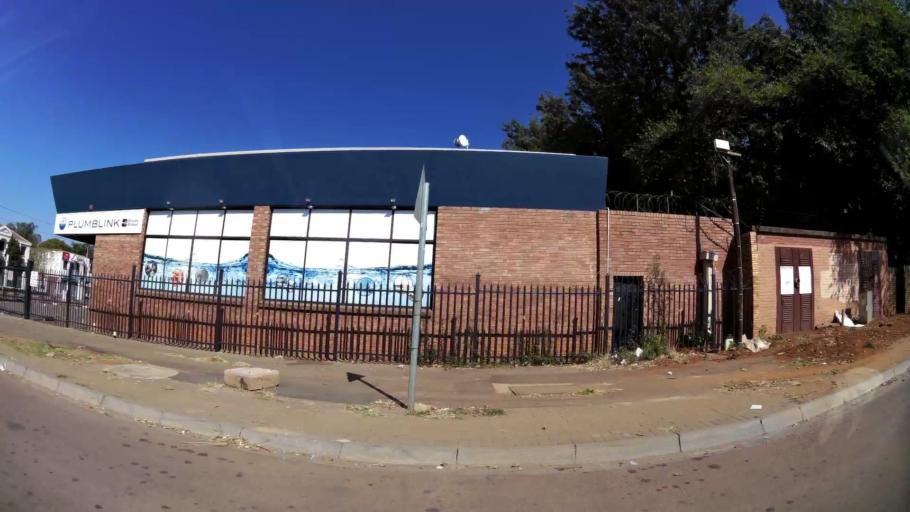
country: ZA
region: Gauteng
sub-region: City of Tshwane Metropolitan Municipality
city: Pretoria
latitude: -25.7584
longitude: 28.2382
